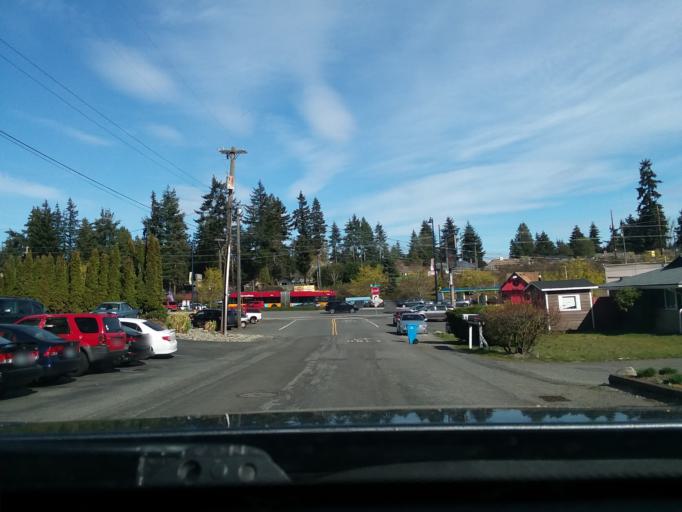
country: US
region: Washington
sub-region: King County
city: Shoreline
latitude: 47.7469
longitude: -122.3467
